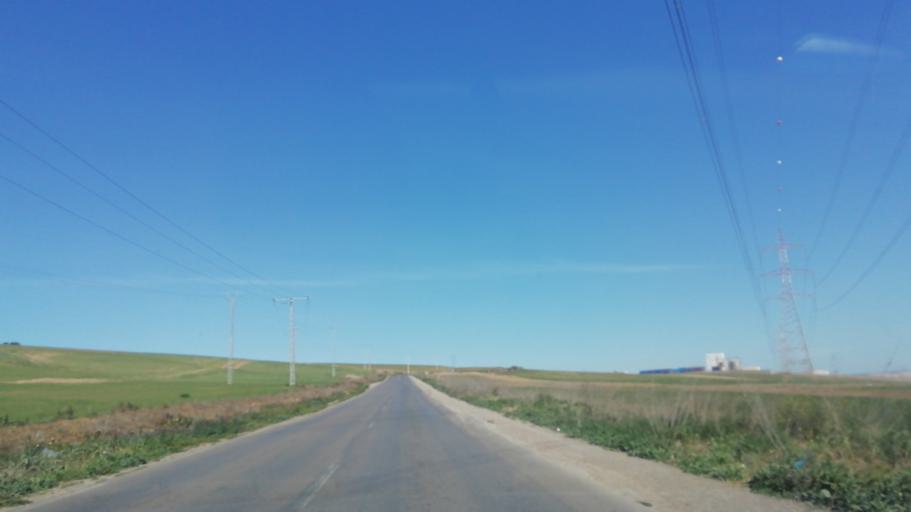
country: DZ
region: Oran
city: Es Senia
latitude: 35.5375
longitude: -0.5846
